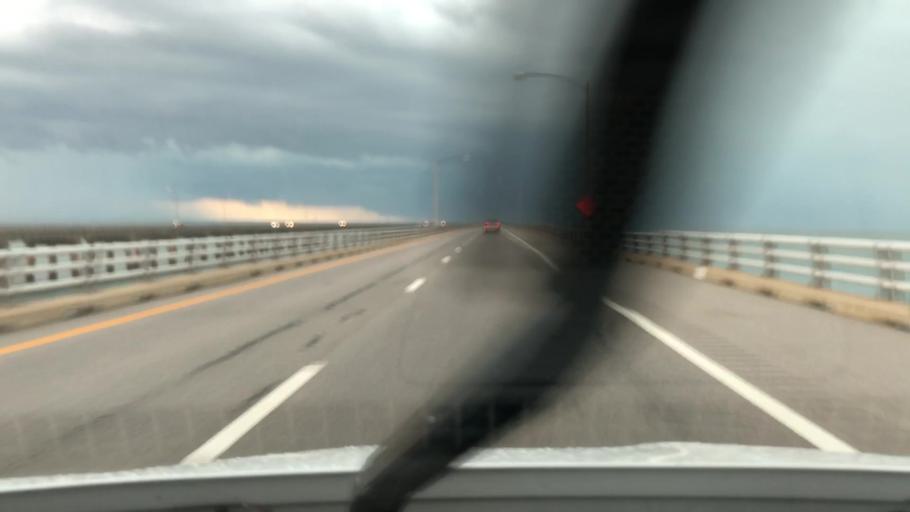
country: US
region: Virginia
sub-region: City of Virginia Beach
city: Virginia Beach
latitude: 37.0205
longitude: -76.0912
